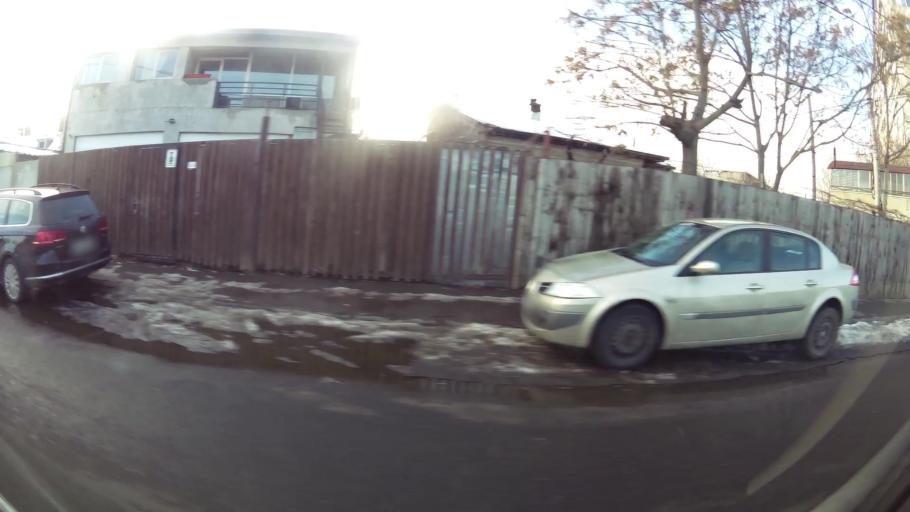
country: RO
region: Bucuresti
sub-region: Municipiul Bucuresti
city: Bucuresti
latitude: 44.3906
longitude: 26.0865
